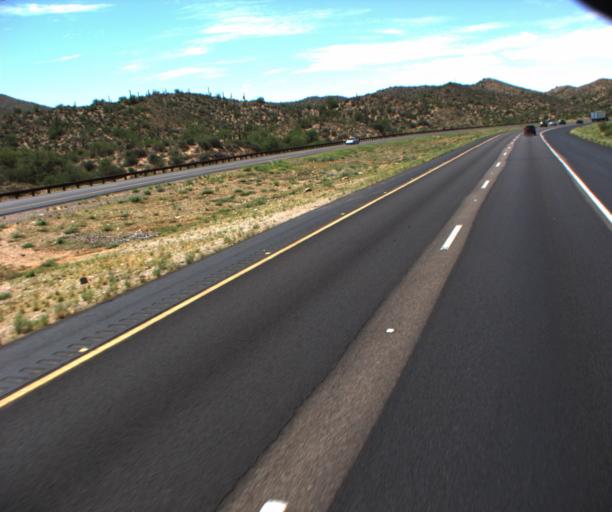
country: US
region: Arizona
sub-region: Pinal County
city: Gold Camp
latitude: 33.2731
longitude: -111.2134
